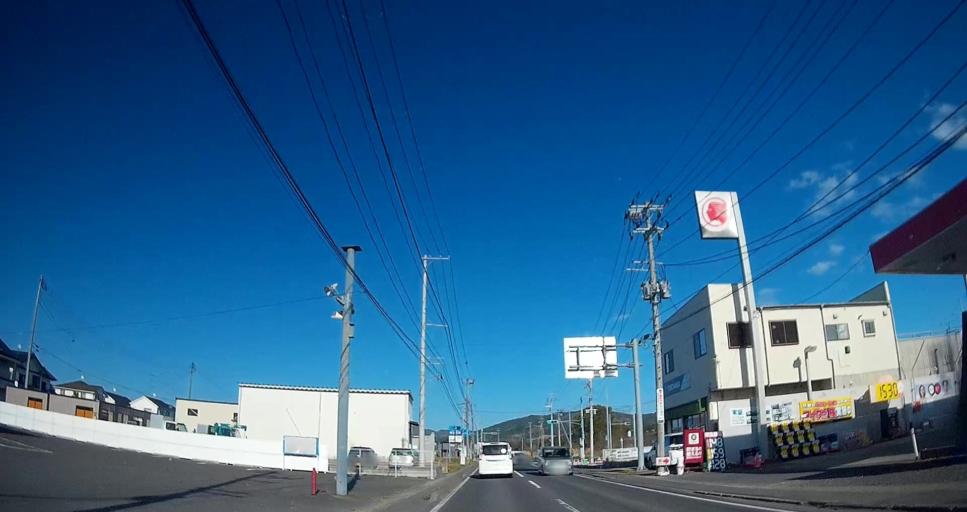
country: JP
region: Miyagi
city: Ishinomaki
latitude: 38.4175
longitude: 141.3446
